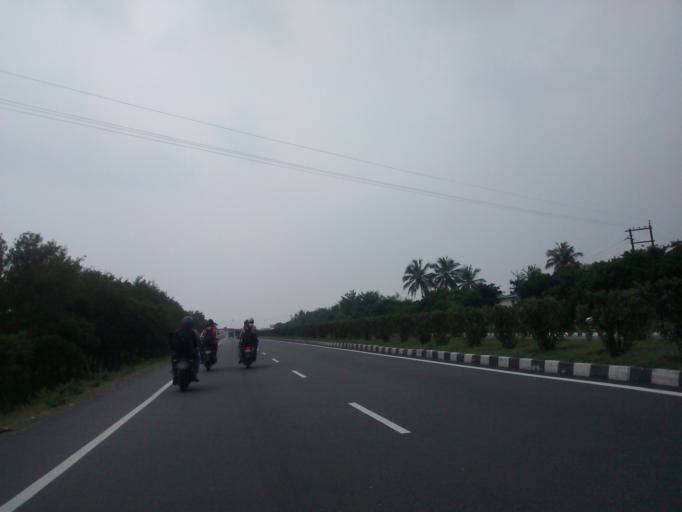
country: IN
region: Tamil Nadu
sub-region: Dharmapuri
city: Dharmapuri
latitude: 12.1643
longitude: 78.1610
